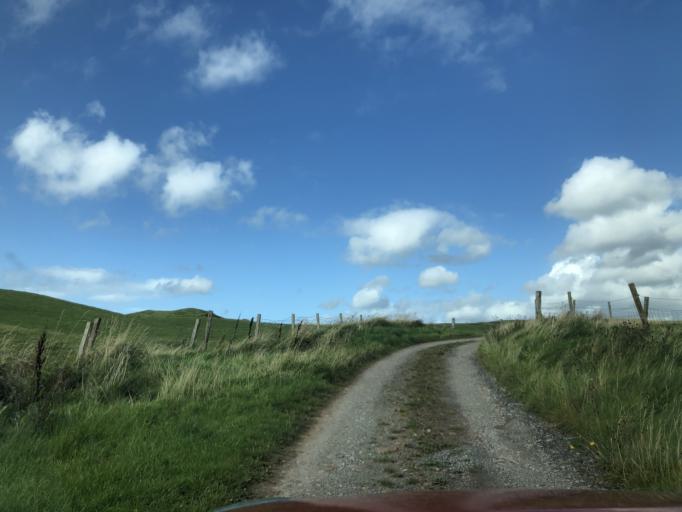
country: GB
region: Scotland
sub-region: Argyll and Bute
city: Campbeltown
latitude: 55.3096
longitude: -5.6082
